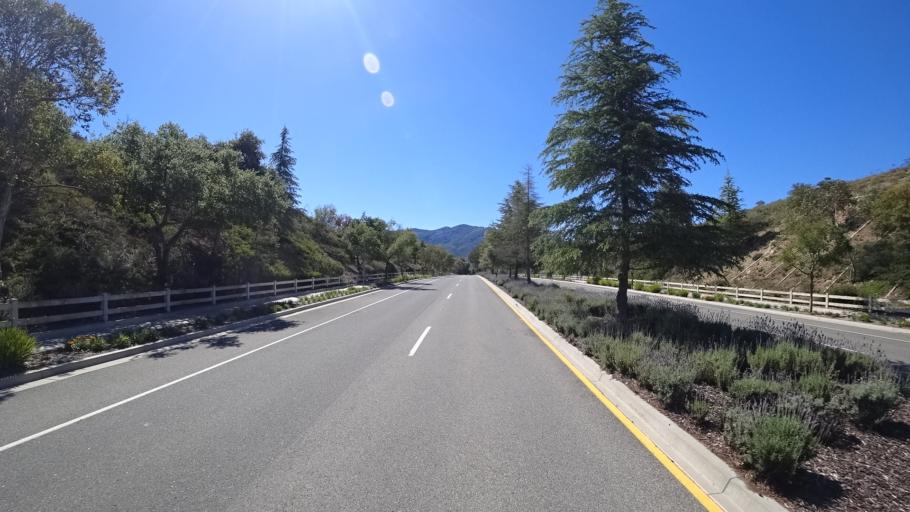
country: US
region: California
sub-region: Ventura County
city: Casa Conejo
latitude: 34.1638
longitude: -118.9716
